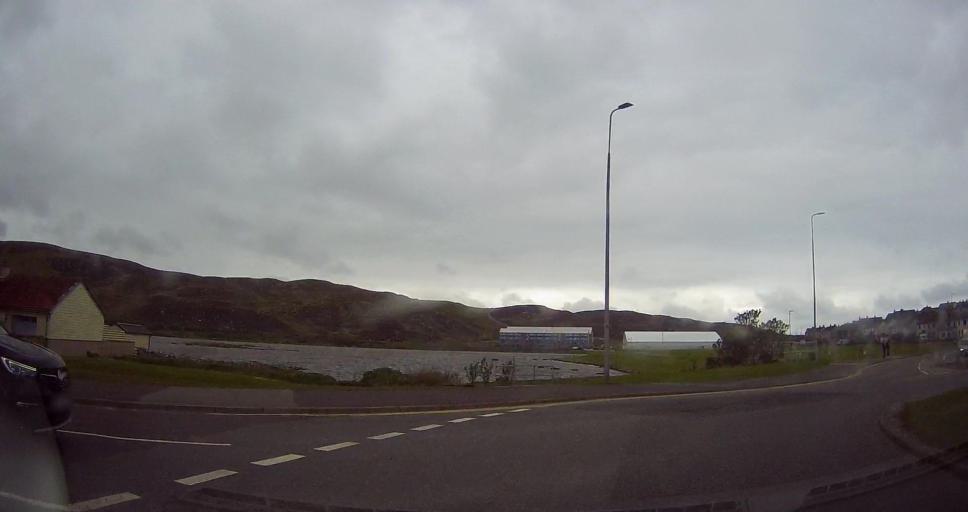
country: GB
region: Scotland
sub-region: Shetland Islands
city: Lerwick
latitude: 60.1487
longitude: -1.1633
